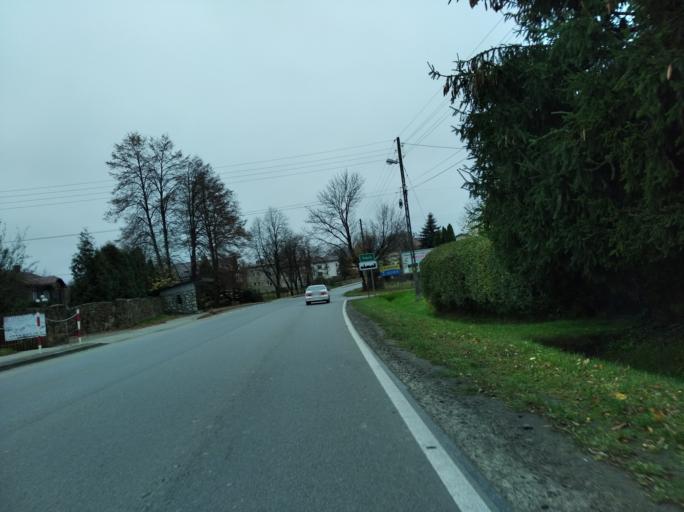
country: PL
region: Subcarpathian Voivodeship
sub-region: Powiat krosnienski
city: Chorkowka
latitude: 49.6692
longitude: 21.6928
